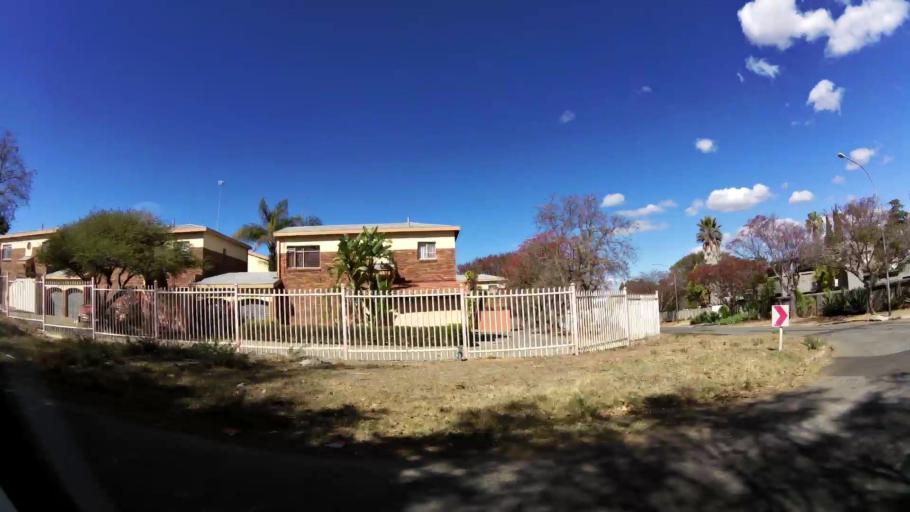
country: ZA
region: Limpopo
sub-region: Capricorn District Municipality
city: Polokwane
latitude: -23.9044
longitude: 29.4837
